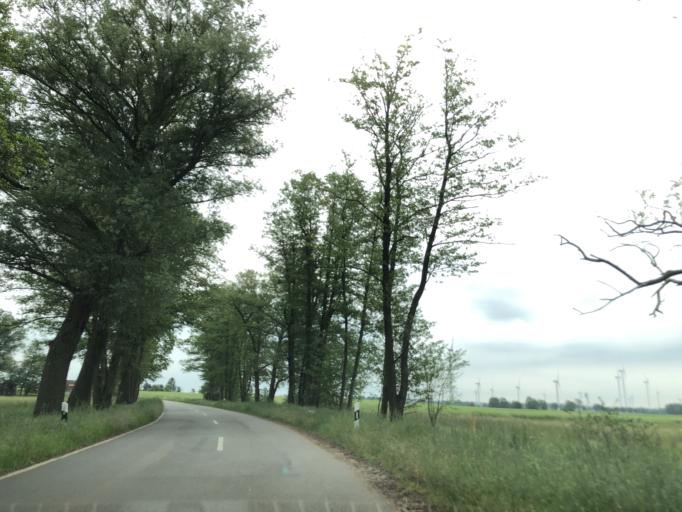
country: DE
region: Brandenburg
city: Breddin
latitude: 52.9559
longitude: 12.1474
